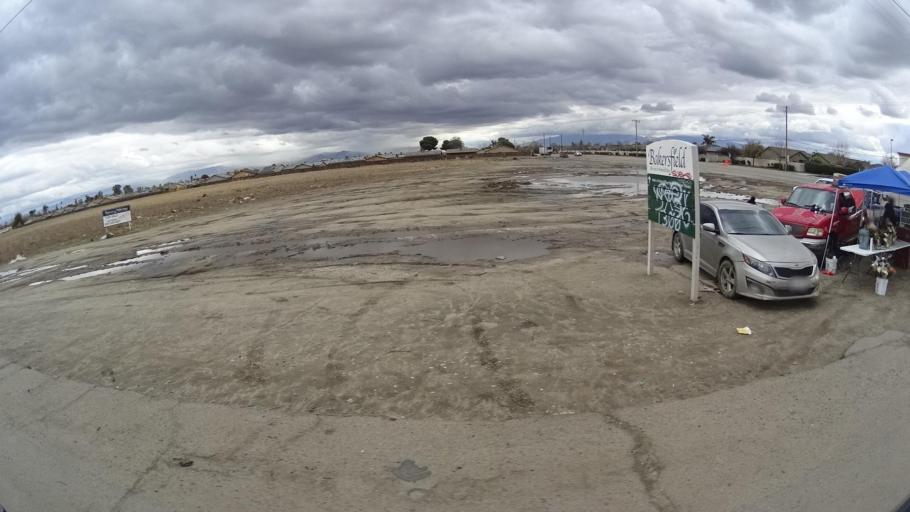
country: US
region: California
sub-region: Kern County
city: Greenfield
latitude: 35.2964
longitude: -119.0026
